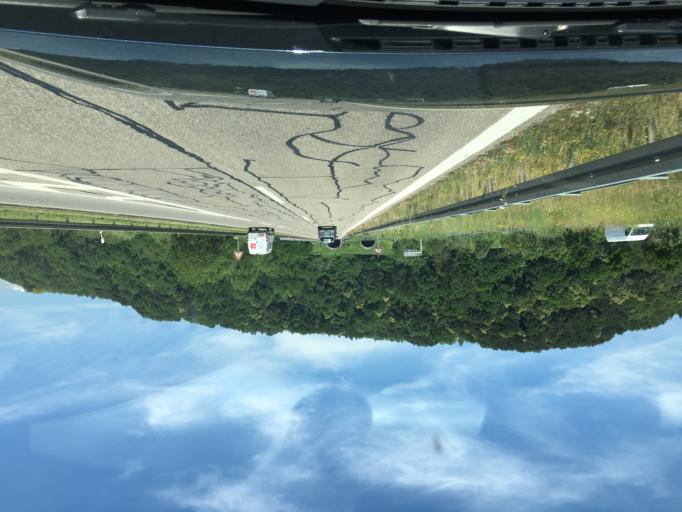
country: DE
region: Baden-Wuerttemberg
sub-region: Freiburg Region
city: Rheinfelden (Baden)
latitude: 47.5675
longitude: 7.7602
